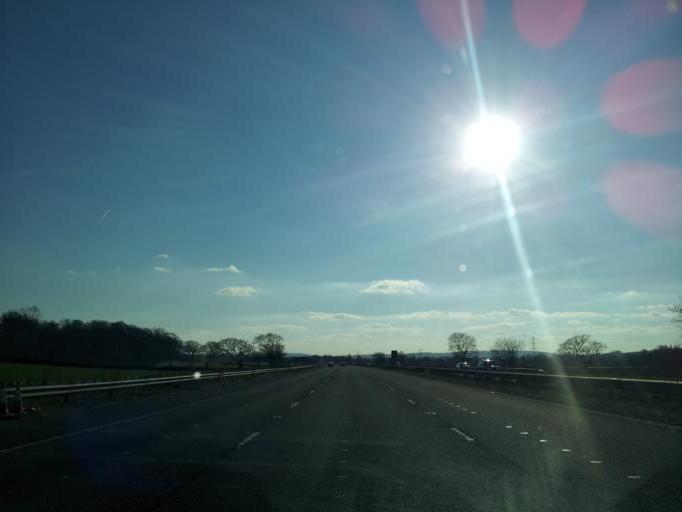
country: GB
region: England
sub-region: Devon
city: Uffculme
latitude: 50.9259
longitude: -3.3435
